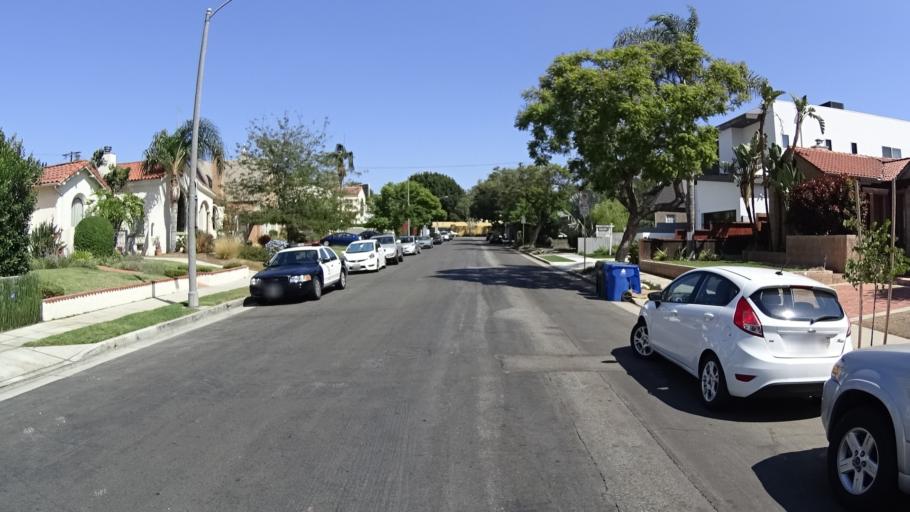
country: US
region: California
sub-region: Los Angeles County
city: West Hollywood
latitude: 34.0676
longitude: -118.3630
